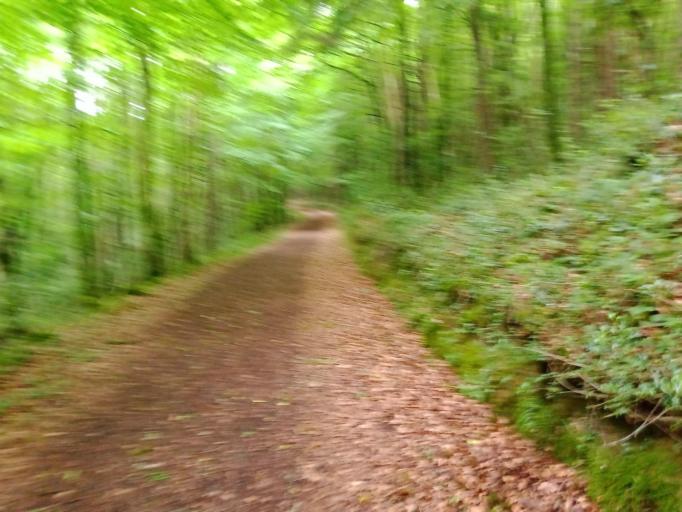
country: IE
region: Leinster
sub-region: Laois
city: Stradbally
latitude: 53.0002
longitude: -7.1177
